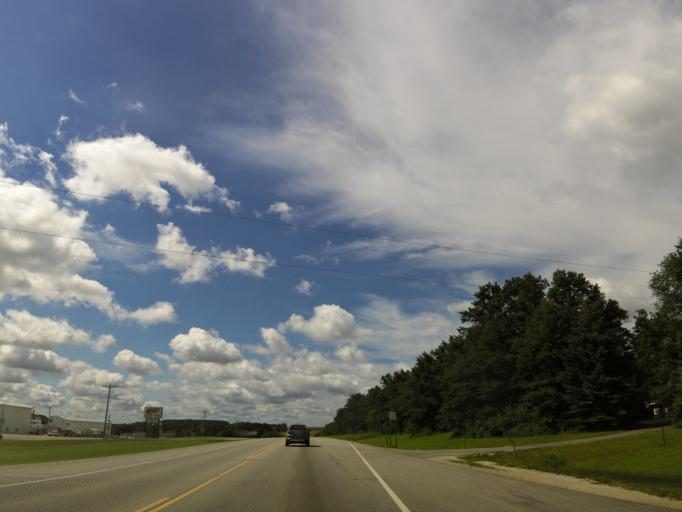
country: US
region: Minnesota
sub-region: Mower County
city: Grand Meadow
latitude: 43.7228
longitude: -92.4794
